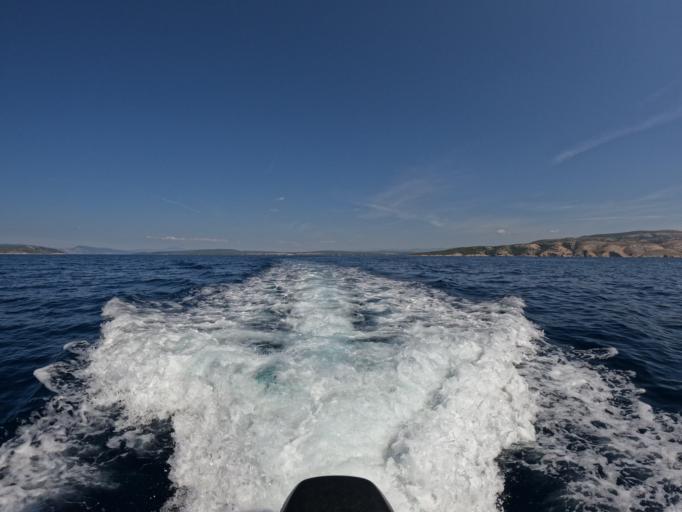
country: HR
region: Primorsko-Goranska
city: Punat
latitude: 44.9501
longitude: 14.6140
